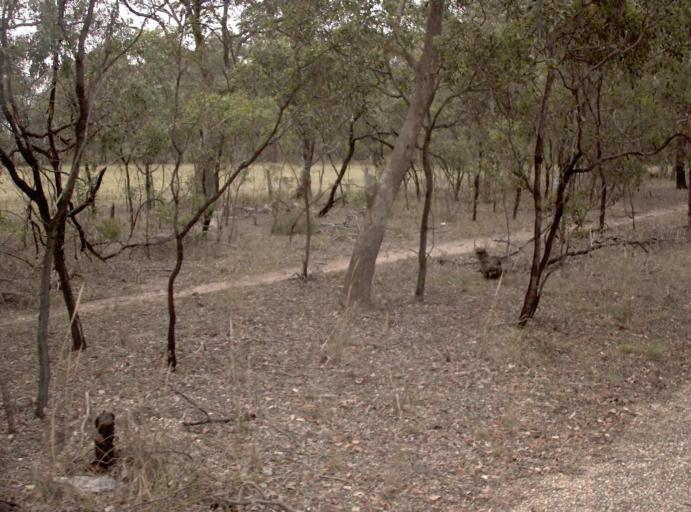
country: AU
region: Victoria
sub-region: Wellington
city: Heyfield
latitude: -37.9570
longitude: 146.7716
